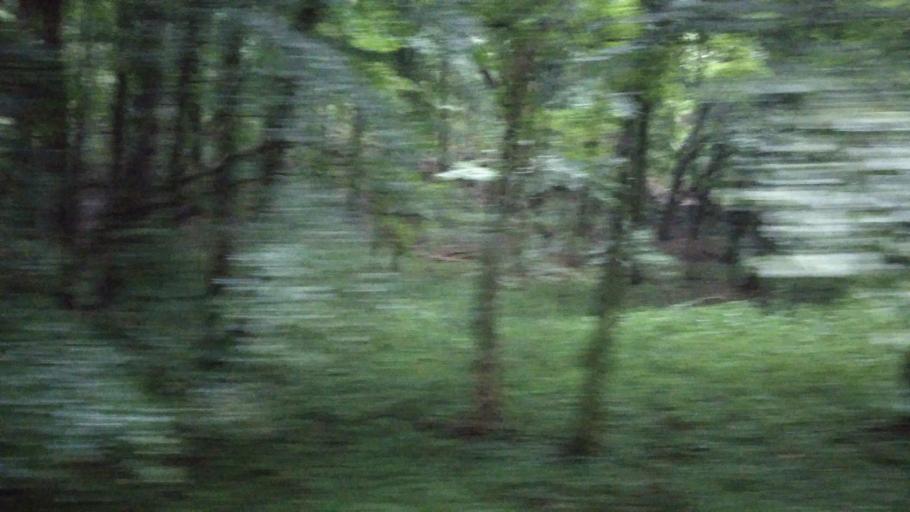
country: HU
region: Pest
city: Szob
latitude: 47.9188
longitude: 18.8691
